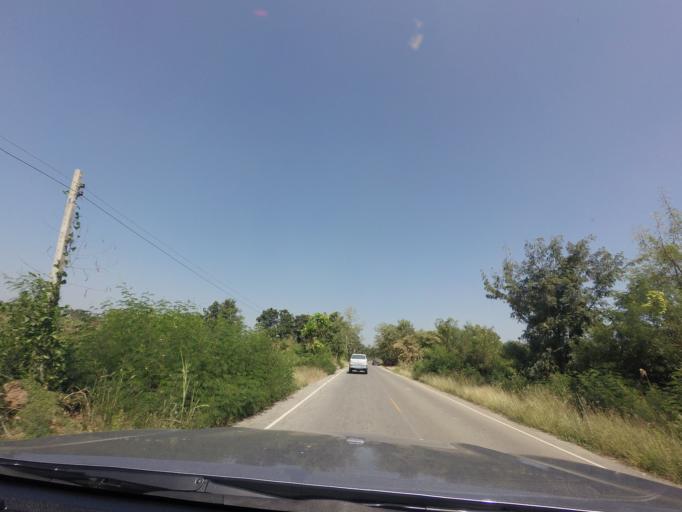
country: TH
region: Sukhothai
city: Si Samrong
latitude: 17.1253
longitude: 99.7816
